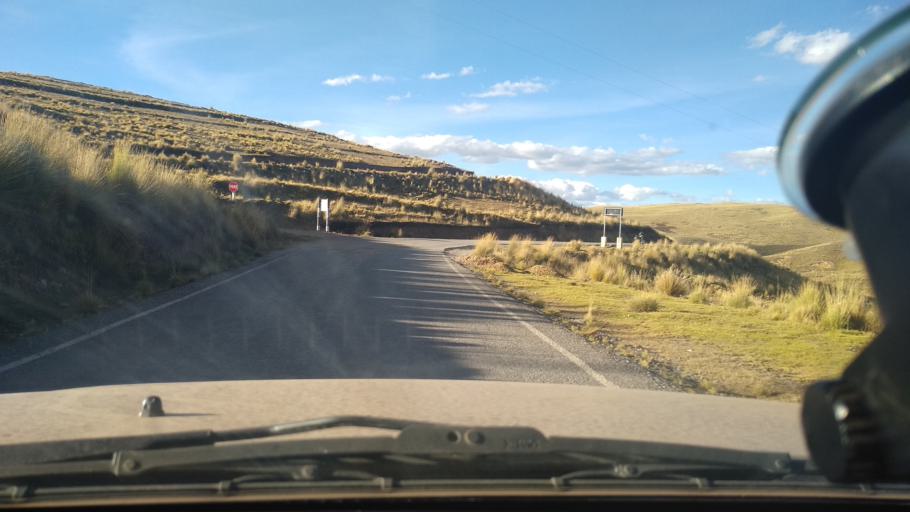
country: PE
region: Cusco
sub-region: Provincia de Canas
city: Ccaquiracunca
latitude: -14.2833
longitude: -71.4507
